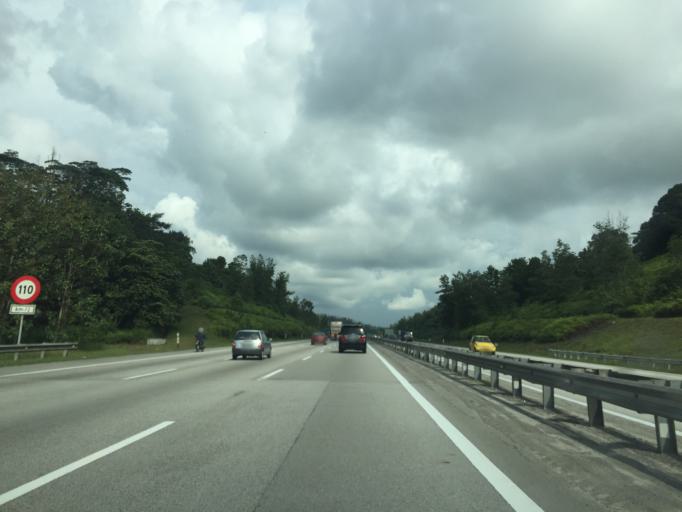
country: MY
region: Selangor
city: Batang Berjuntai
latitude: 3.5845
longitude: 101.5219
